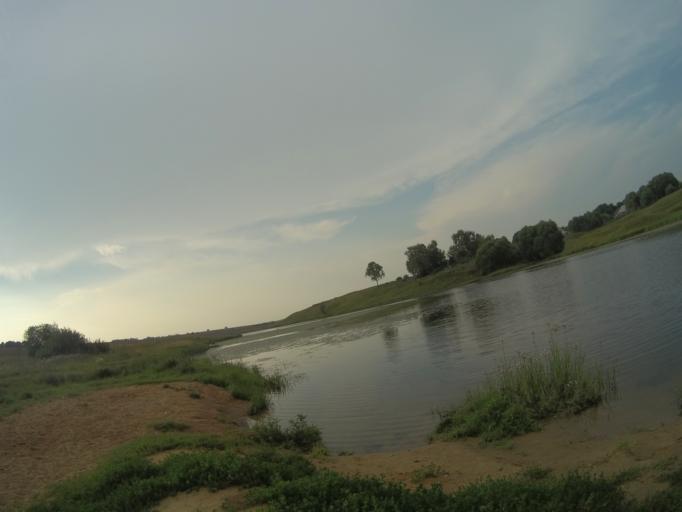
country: RU
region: Vladimir
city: Stavrovo
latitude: 56.3248
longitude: 40.1134
